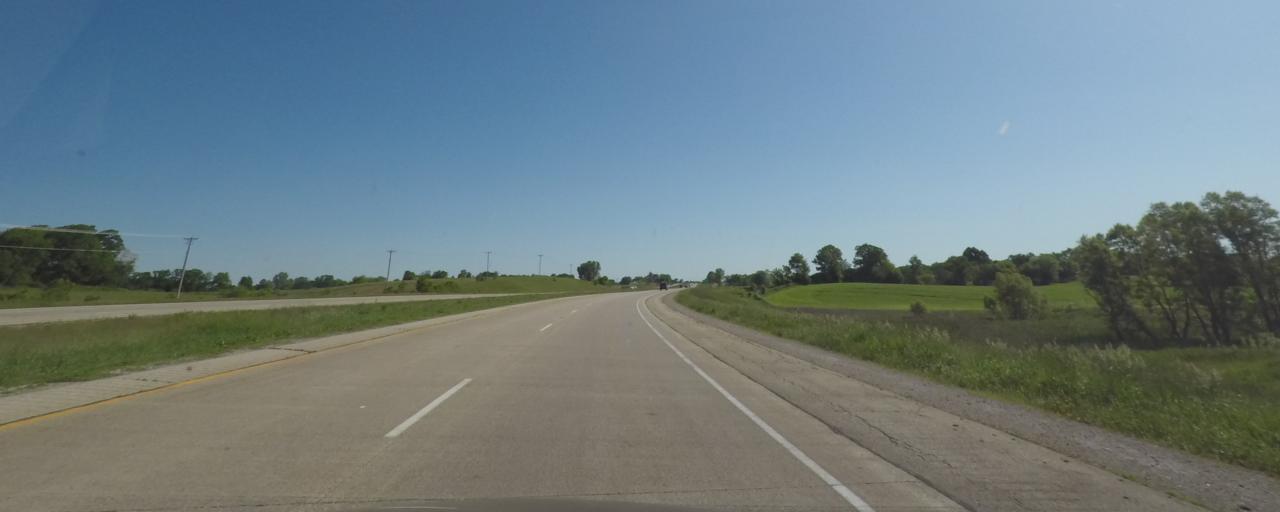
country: US
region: Wisconsin
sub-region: Fond du Lac County
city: Waupun
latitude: 43.5658
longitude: -88.7744
